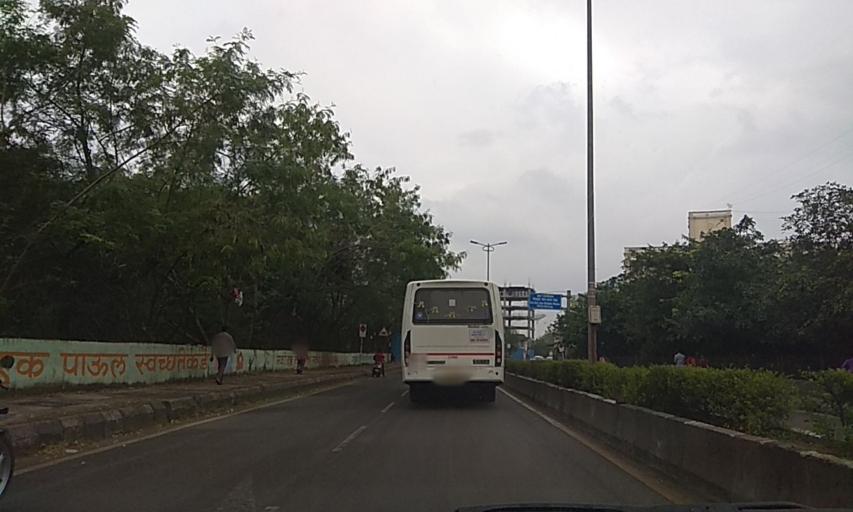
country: IN
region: Maharashtra
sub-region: Pune Division
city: Lohogaon
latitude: 18.5660
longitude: 73.9067
